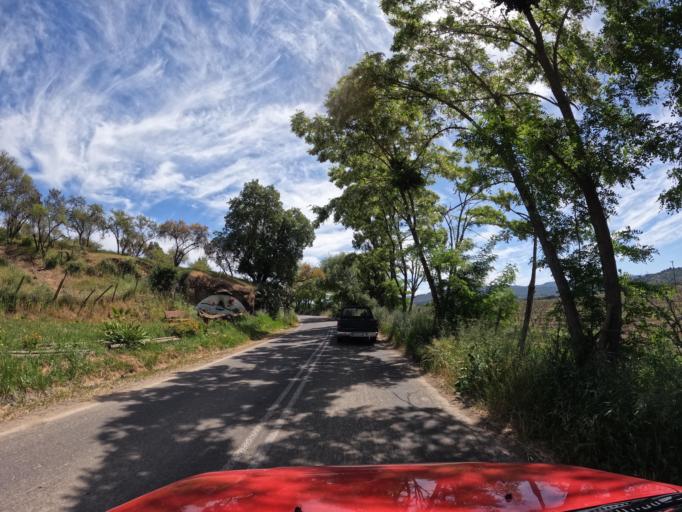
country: CL
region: Maule
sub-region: Provincia de Talca
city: Talca
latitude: -34.9893
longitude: -71.8351
